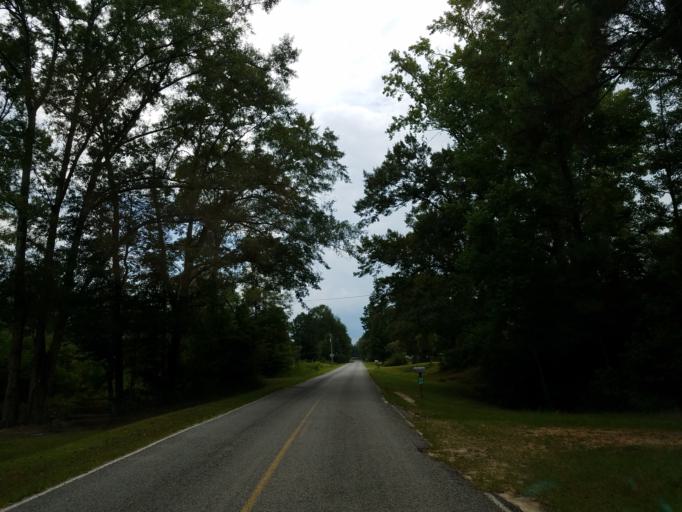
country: US
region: Mississippi
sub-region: Perry County
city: Richton
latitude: 31.3573
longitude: -88.8168
